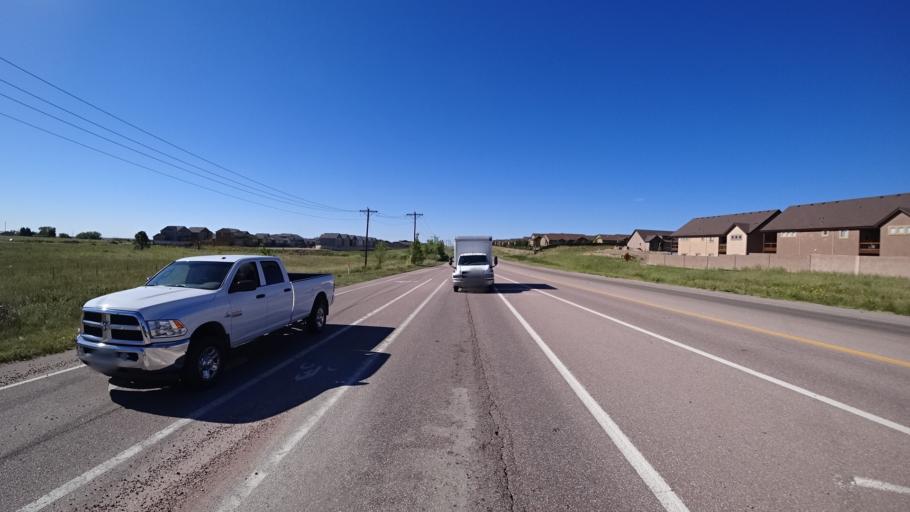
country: US
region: Colorado
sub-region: El Paso County
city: Cimarron Hills
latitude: 38.9260
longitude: -104.6827
